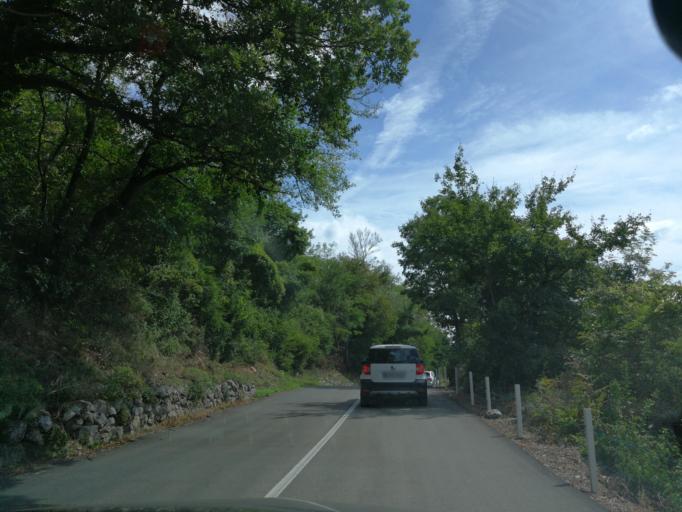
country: HR
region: Primorsko-Goranska
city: Punat
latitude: 45.0825
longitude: 14.6493
